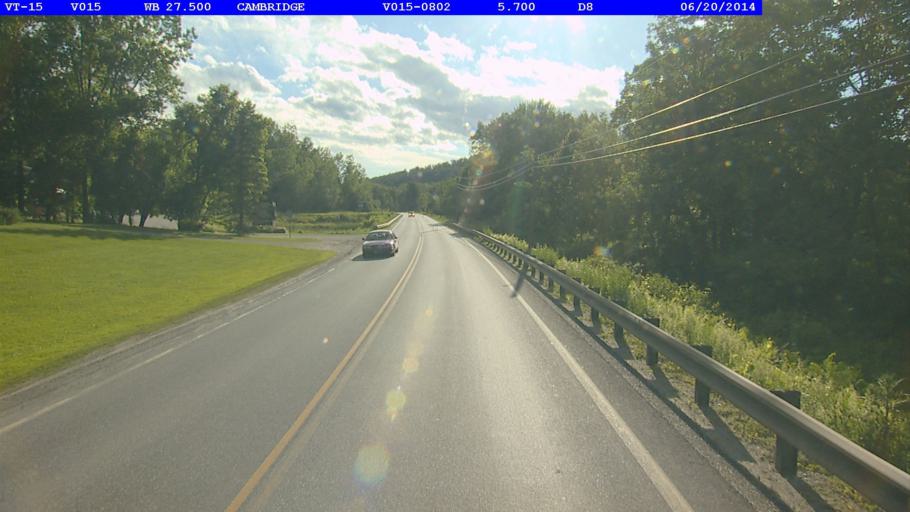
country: US
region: Vermont
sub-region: Lamoille County
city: Johnson
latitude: 44.6501
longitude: -72.8189
